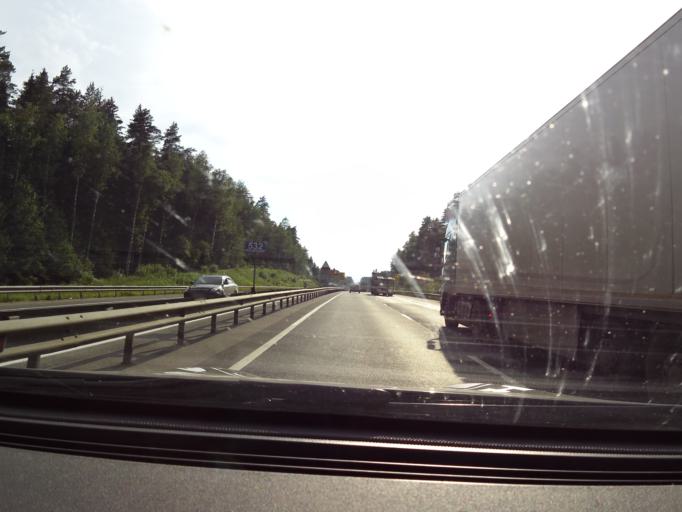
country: RU
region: Vladimir
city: Stepantsevo
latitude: 56.2296
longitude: 41.7170
